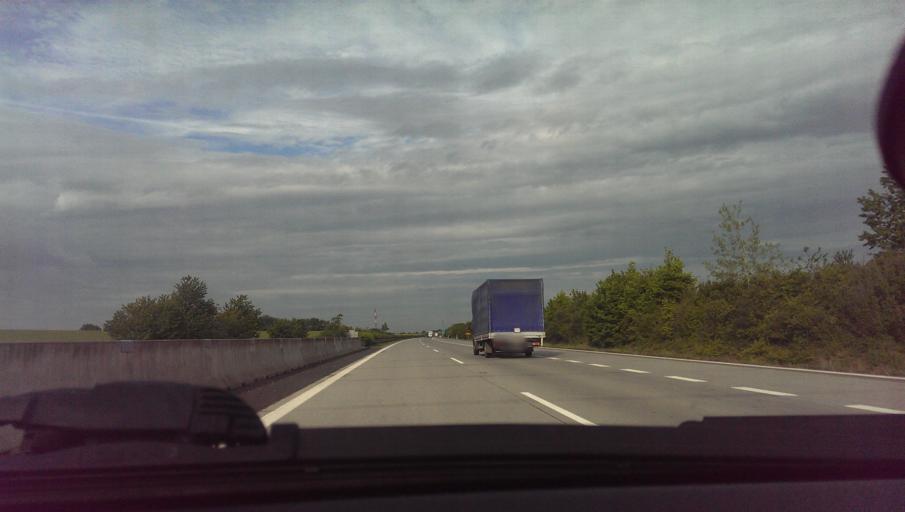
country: CZ
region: Olomoucky
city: Nezamyslice
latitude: 49.3214
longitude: 17.1949
